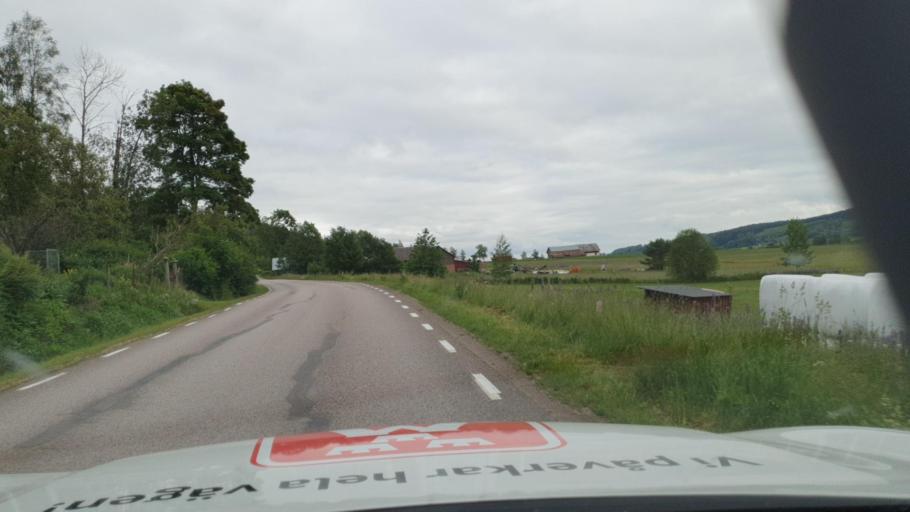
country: SE
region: Vaermland
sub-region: Kils Kommun
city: Kil
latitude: 59.6283
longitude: 13.3230
